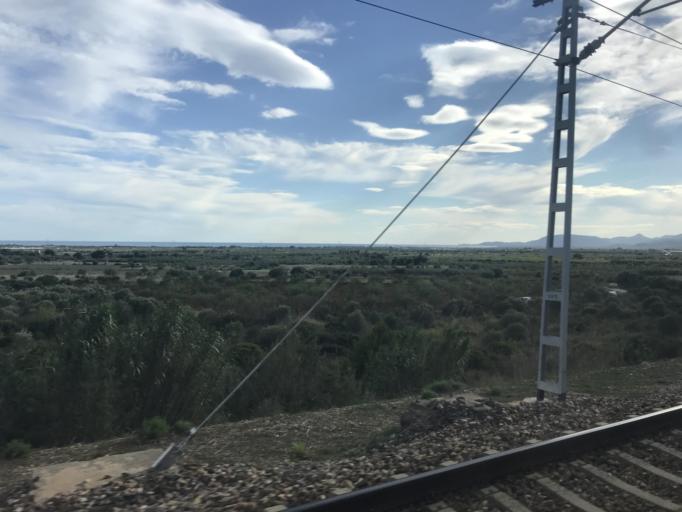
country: ES
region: Valencia
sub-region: Provincia de Castello
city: Alcoceber
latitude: 40.2495
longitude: 0.2435
